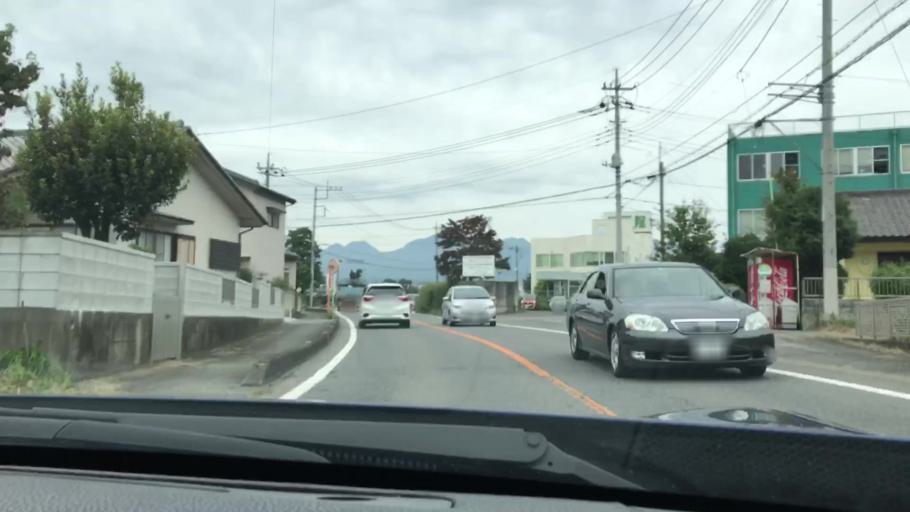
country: JP
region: Gunma
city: Kanekomachi
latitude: 36.3990
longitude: 138.9912
